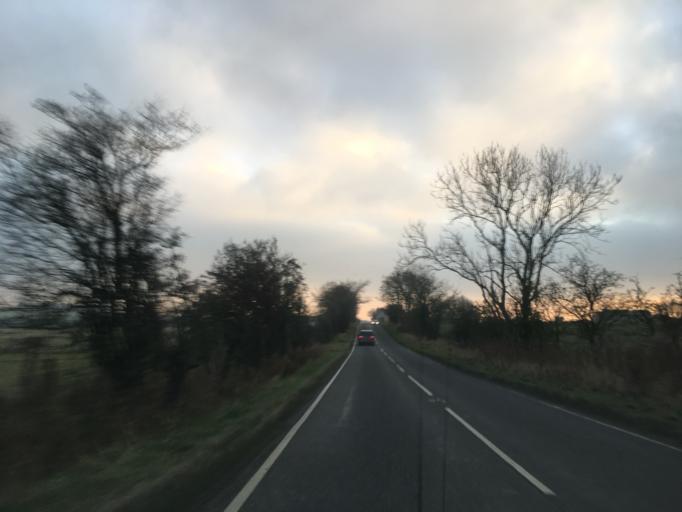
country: GB
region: Scotland
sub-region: Fife
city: Strathkinness
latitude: 56.2716
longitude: -2.8493
